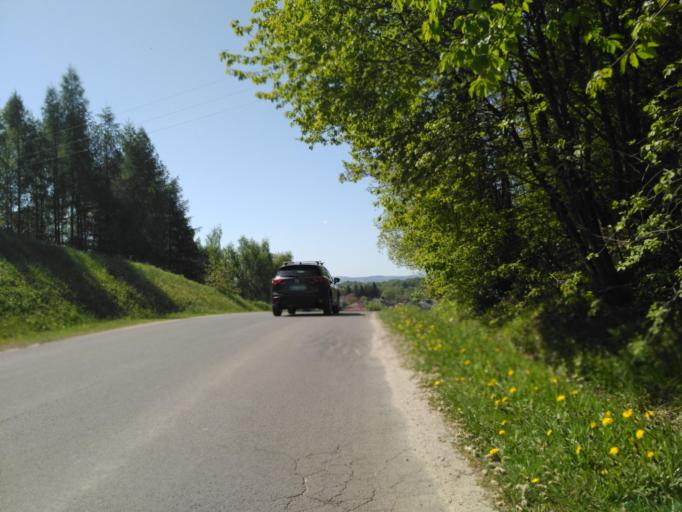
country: PL
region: Subcarpathian Voivodeship
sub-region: Krosno
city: Krosno
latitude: 49.6922
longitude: 21.7903
